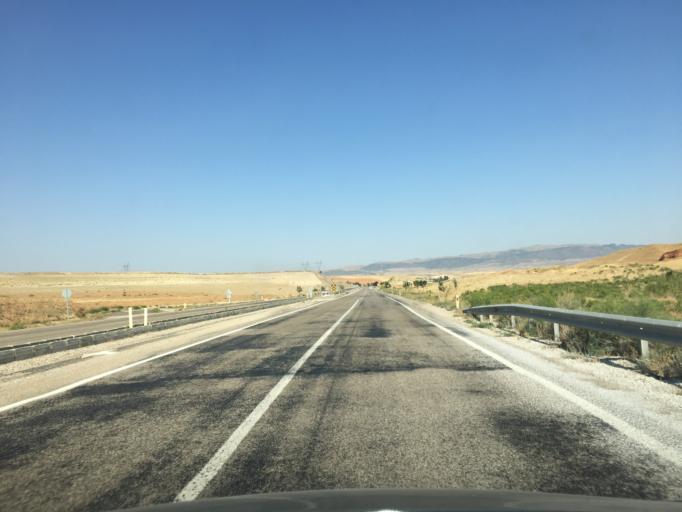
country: TR
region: Kirikkale
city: Karakecili
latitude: 39.5605
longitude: 33.3003
